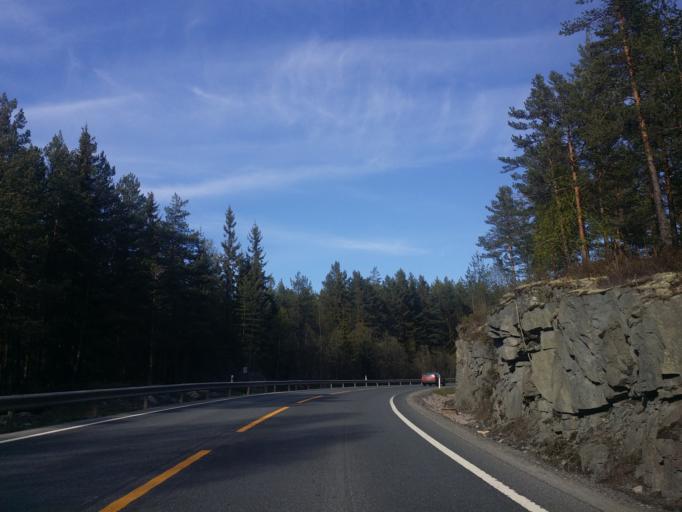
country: NO
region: Telemark
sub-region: Notodden
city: Notodden
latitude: 59.5844
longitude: 9.3008
